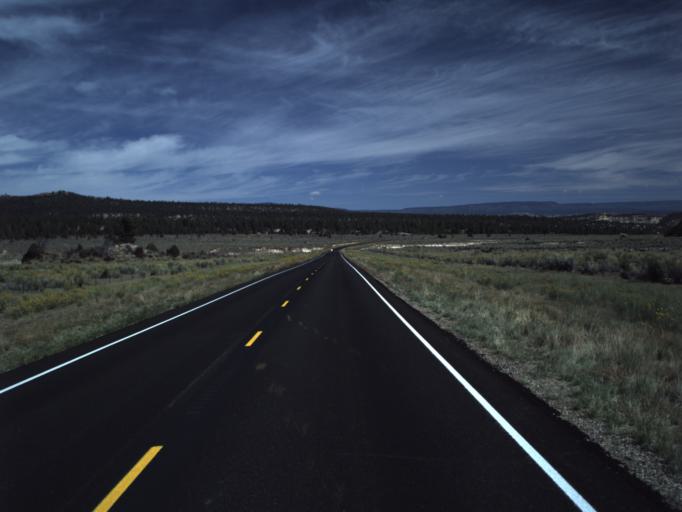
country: US
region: Utah
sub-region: Garfield County
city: Panguitch
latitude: 37.6660
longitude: -111.8314
